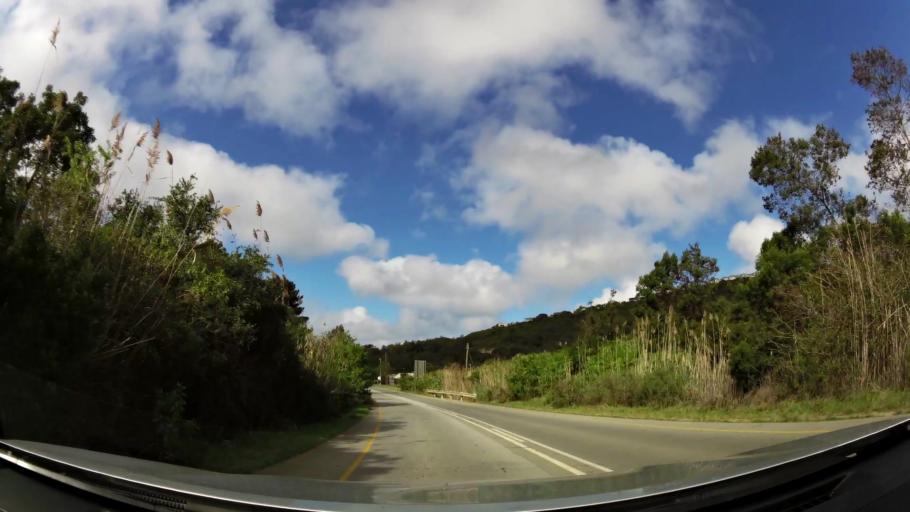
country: ZA
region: Western Cape
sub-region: Eden District Municipality
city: Plettenberg Bay
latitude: -34.0619
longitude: 23.3556
